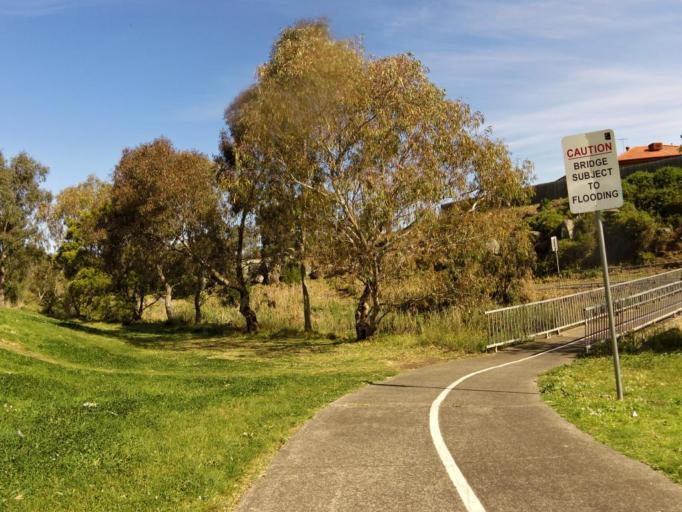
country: AU
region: Victoria
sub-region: Brimbank
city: Sunshine West
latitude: -37.7965
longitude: 144.8218
